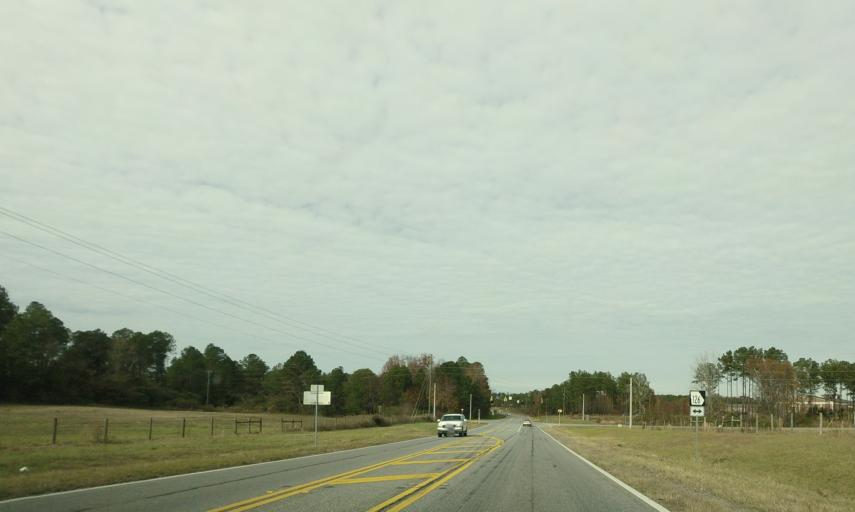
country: US
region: Georgia
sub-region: Bleckley County
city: Cochran
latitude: 32.3965
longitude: -83.3280
